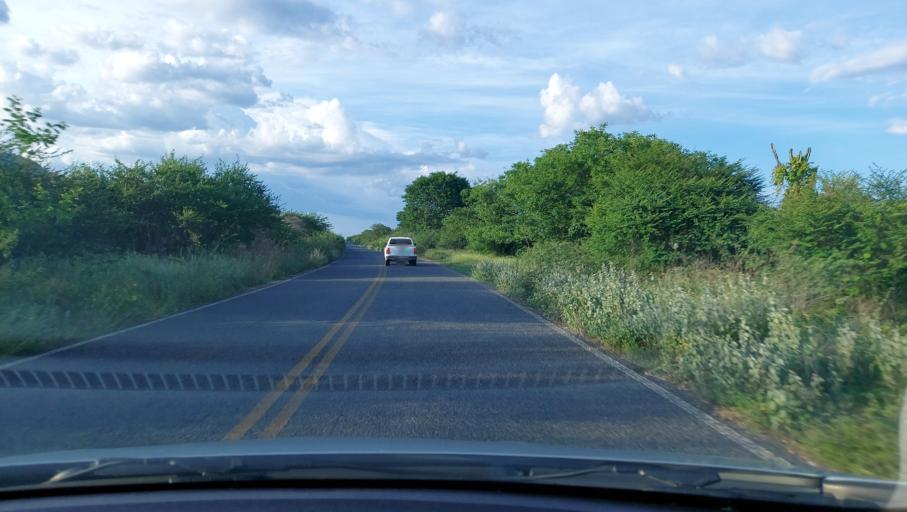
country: BR
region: Bahia
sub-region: Oliveira Dos Brejinhos
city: Beira Rio
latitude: -12.1923
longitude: -42.5373
